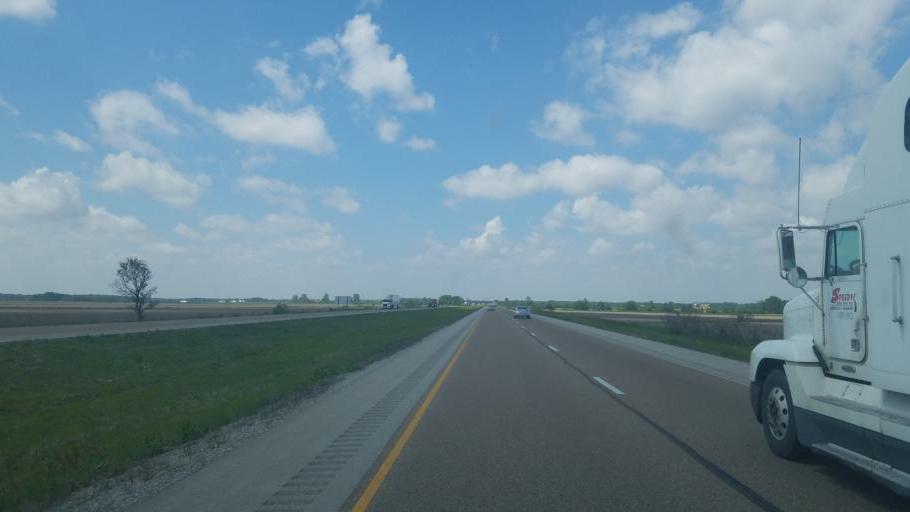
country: US
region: Illinois
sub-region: Clark County
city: Casey
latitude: 39.3076
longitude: -88.0150
